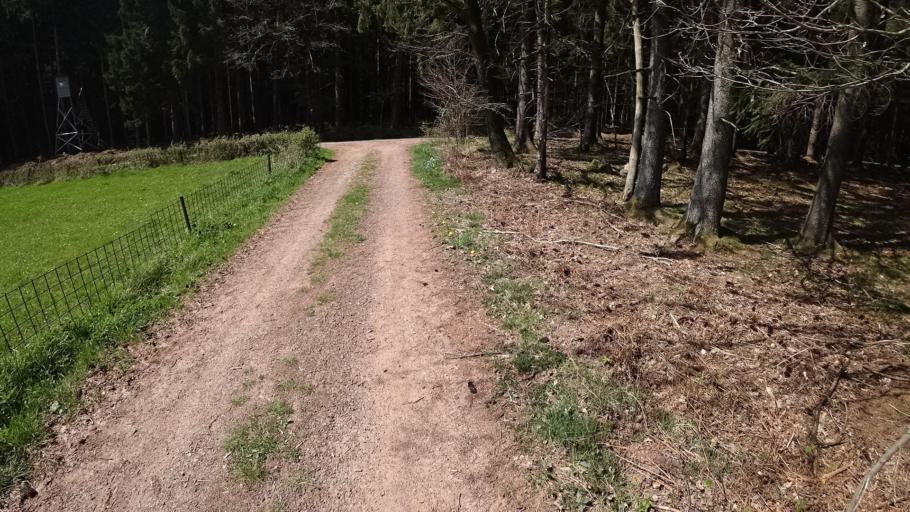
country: DE
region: Rheinland-Pfalz
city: Gusenburg
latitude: 49.6336
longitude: 6.8860
